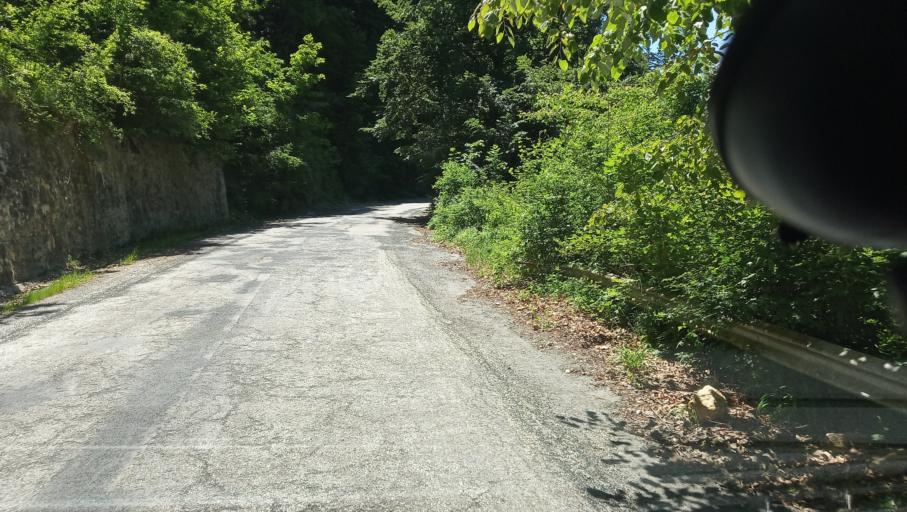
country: RO
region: Mehedinti
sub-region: Comuna Isverna
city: Isverna
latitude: 45.0003
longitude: 22.5340
